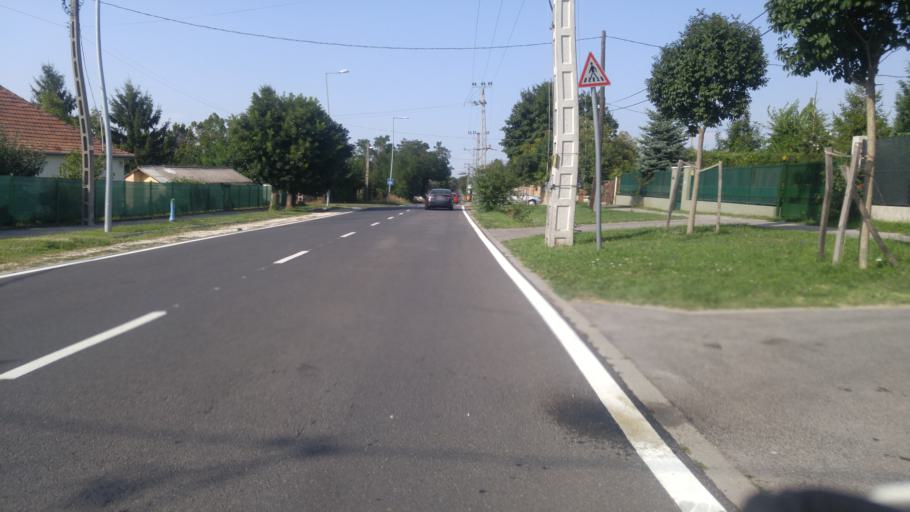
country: HU
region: Budapest
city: Budapest XVII. keruelet
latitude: 47.4596
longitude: 19.2462
